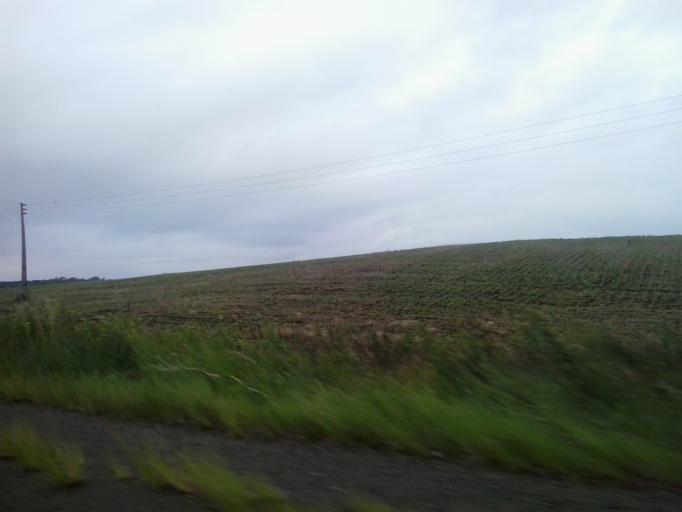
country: BR
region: Rio Grande do Sul
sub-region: Santa Maria
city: Santa Maria
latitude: -29.7228
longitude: -53.3671
